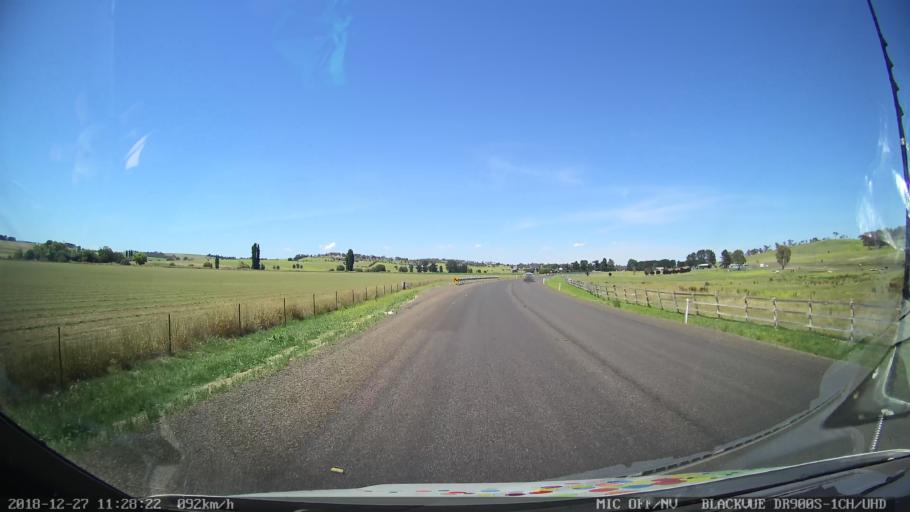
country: AU
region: New South Wales
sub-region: Bathurst Regional
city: Perthville
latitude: -33.4753
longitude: 149.5640
